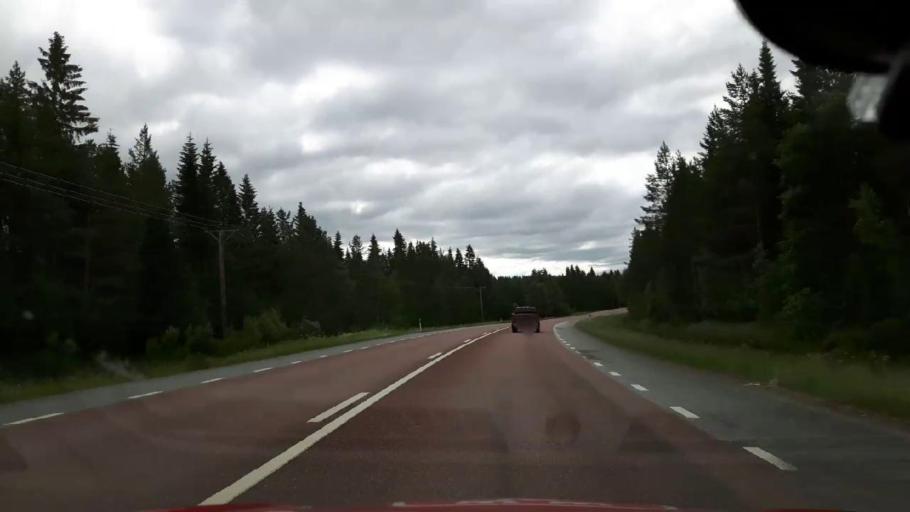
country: SE
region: Jaemtland
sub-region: Braecke Kommun
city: Braecke
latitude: 62.7714
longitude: 15.4028
